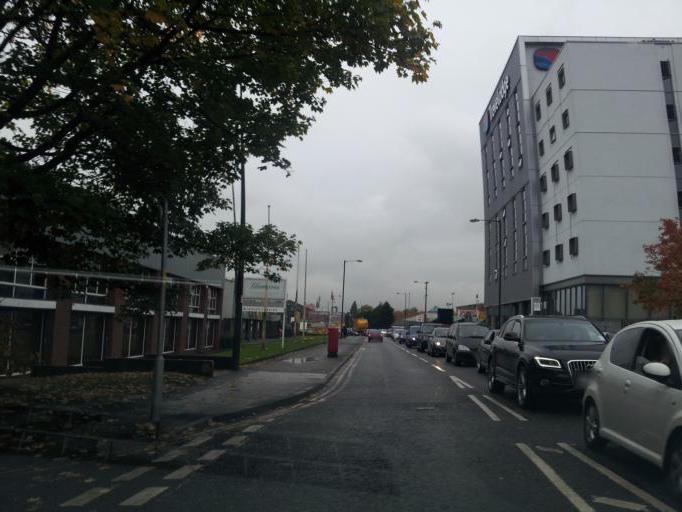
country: GB
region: England
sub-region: Manchester
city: Cheetham Hill
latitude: 53.4896
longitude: -2.2466
